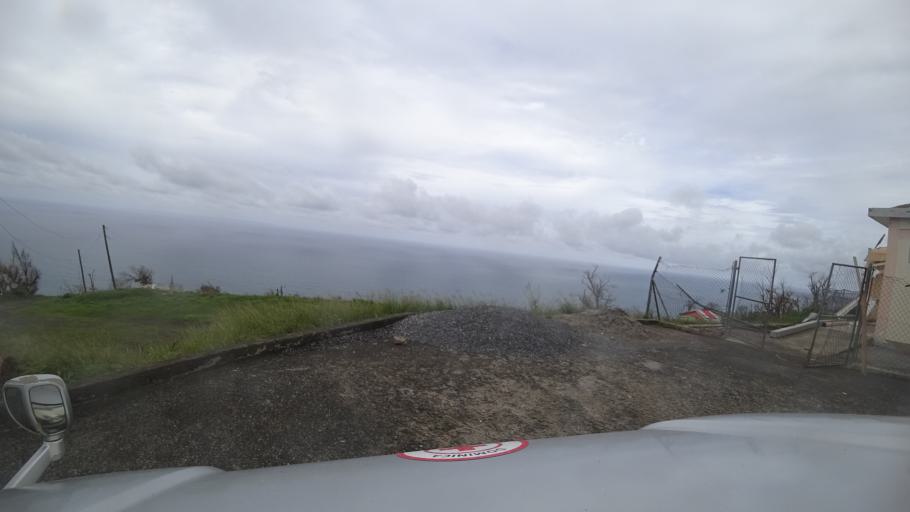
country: DM
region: Saint John
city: Portsmouth
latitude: 15.6294
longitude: -61.4217
